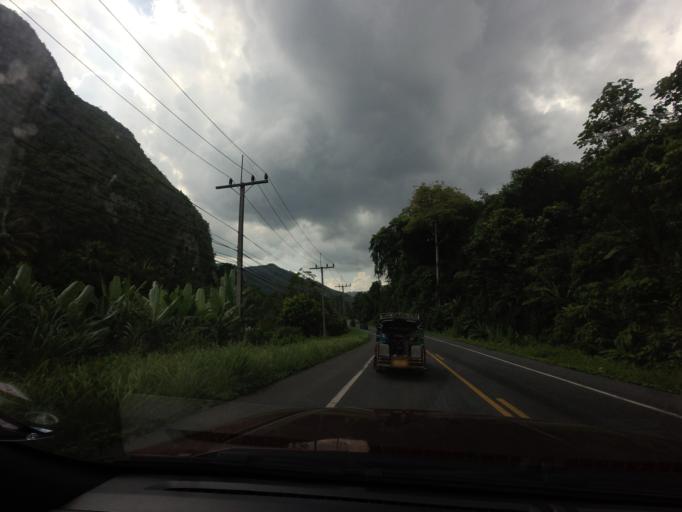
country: TH
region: Yala
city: Than To
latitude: 6.2108
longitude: 101.1671
